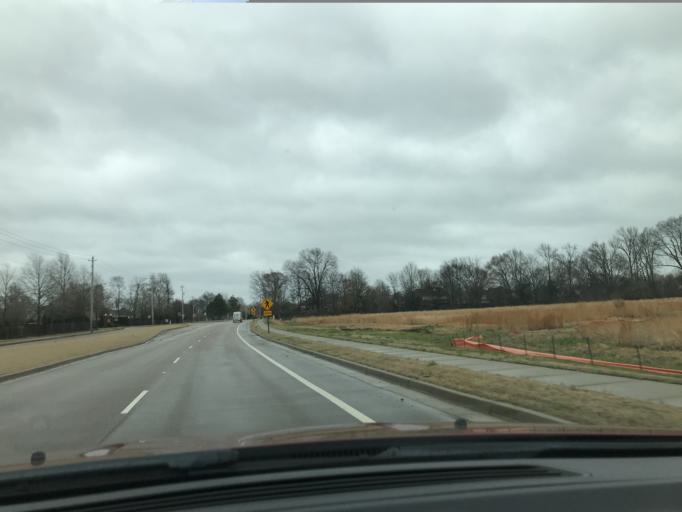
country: US
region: Tennessee
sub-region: Shelby County
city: Collierville
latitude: 35.0864
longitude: -89.7037
